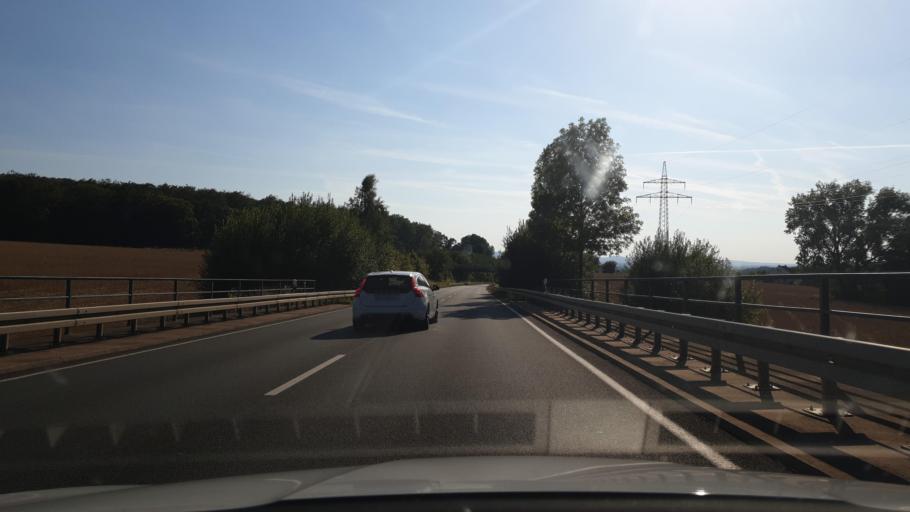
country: DE
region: North Rhine-Westphalia
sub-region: Regierungsbezirk Detmold
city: Lemgo
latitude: 51.9963
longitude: 8.8971
